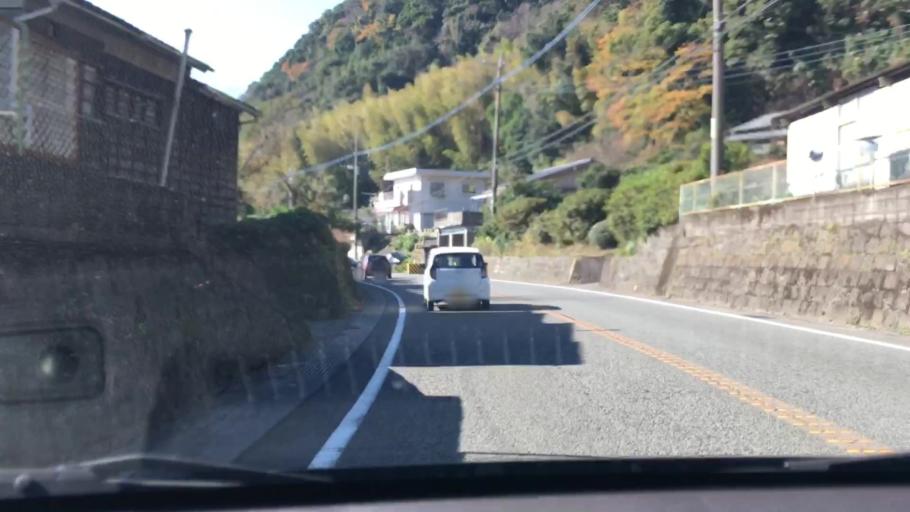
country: JP
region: Kagoshima
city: Kagoshima-shi
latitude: 31.6229
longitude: 130.5864
